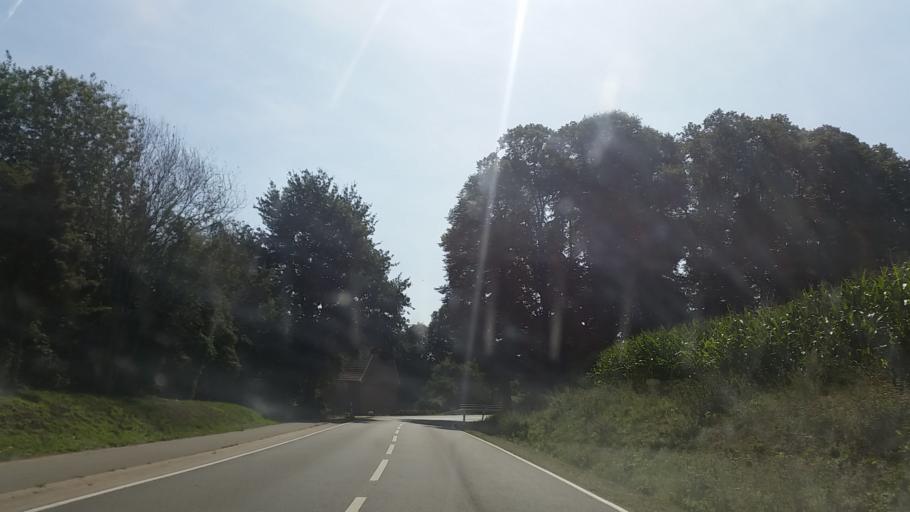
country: DE
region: Lower Saxony
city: Ankum
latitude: 52.5305
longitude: 7.8927
